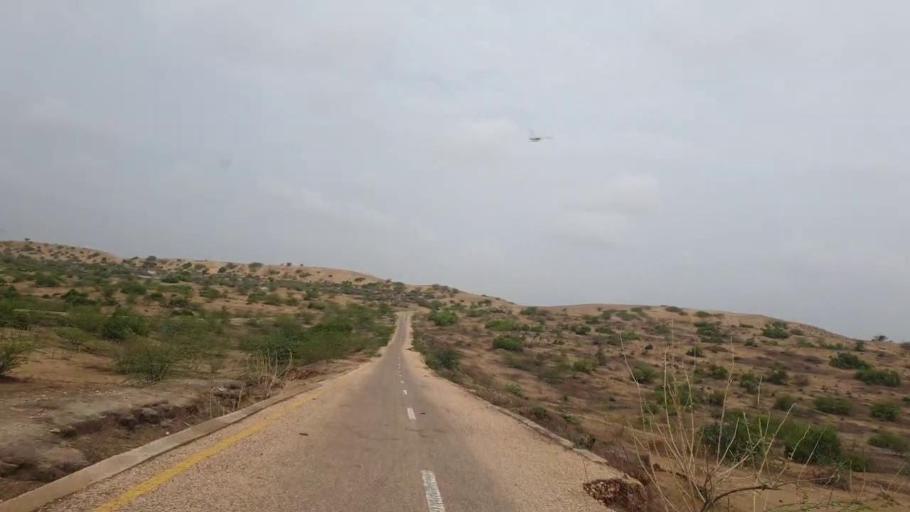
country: PK
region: Sindh
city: Naukot
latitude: 24.6249
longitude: 69.3689
